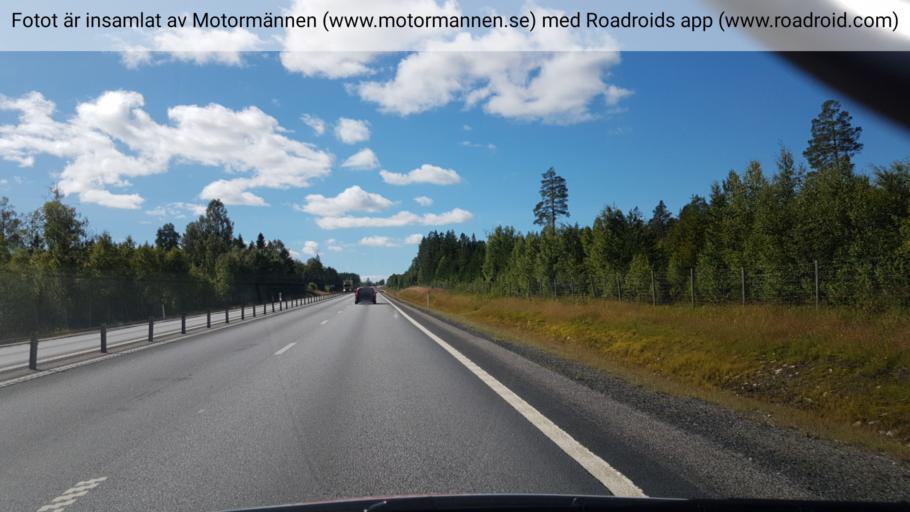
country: SE
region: Vaesterbotten
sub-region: Umea Kommun
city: Hoernefors
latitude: 63.6622
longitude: 19.9634
